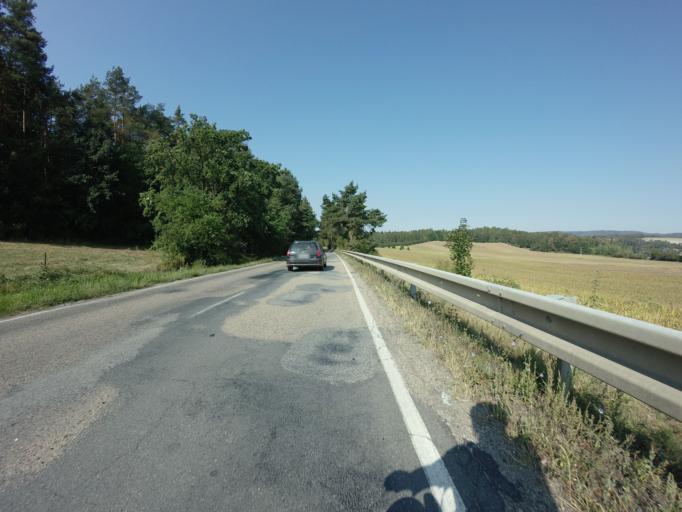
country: CZ
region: Central Bohemia
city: Tynec nad Sazavou
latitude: 49.8268
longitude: 14.6142
